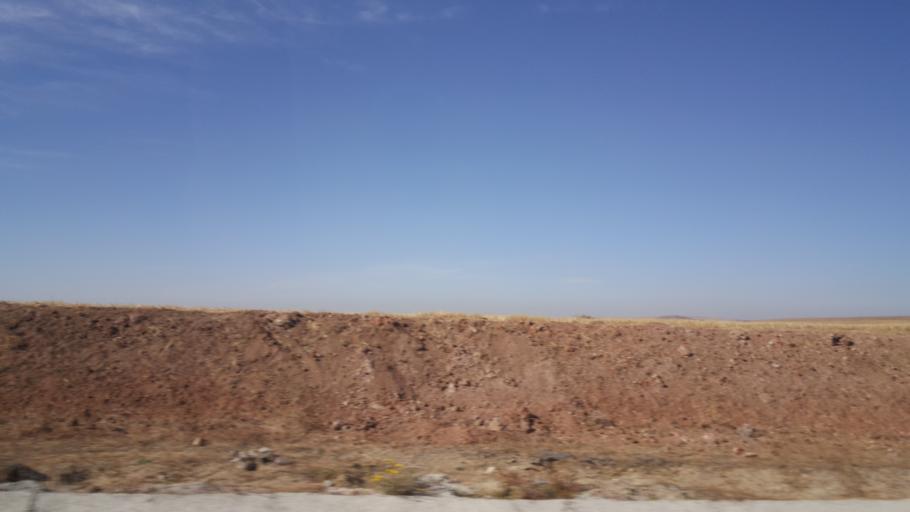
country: TR
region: Ankara
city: Haymana
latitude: 39.4945
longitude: 32.5599
